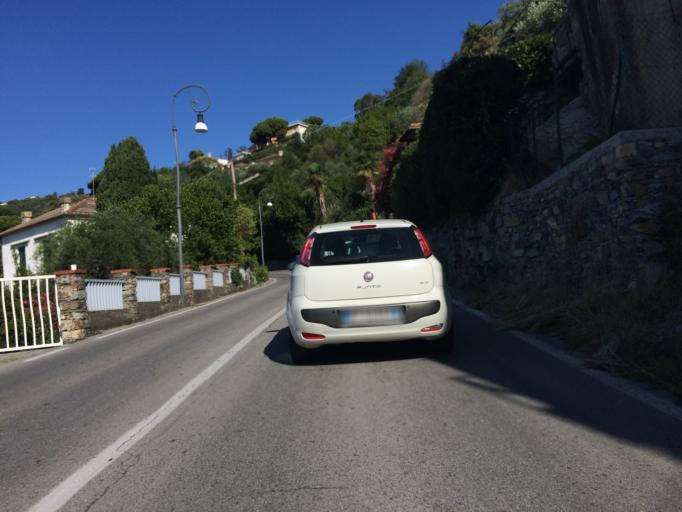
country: IT
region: Liguria
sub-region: Provincia di Genova
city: Rapallo
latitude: 44.3445
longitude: 9.2193
